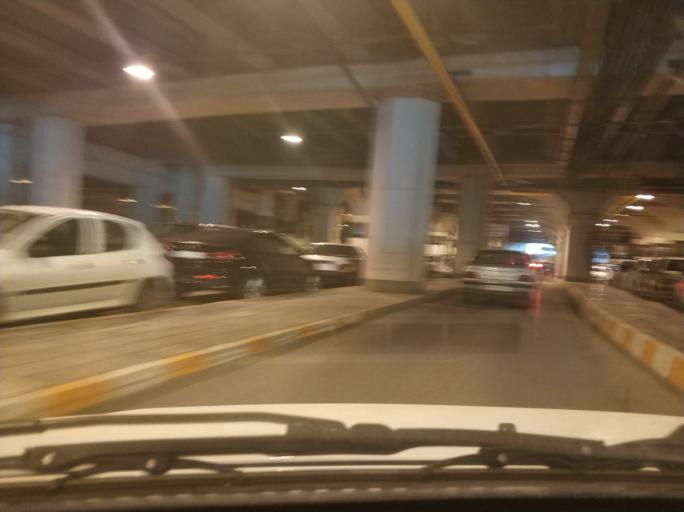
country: IR
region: Razavi Khorasan
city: Mashhad
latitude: 36.2902
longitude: 59.6138
